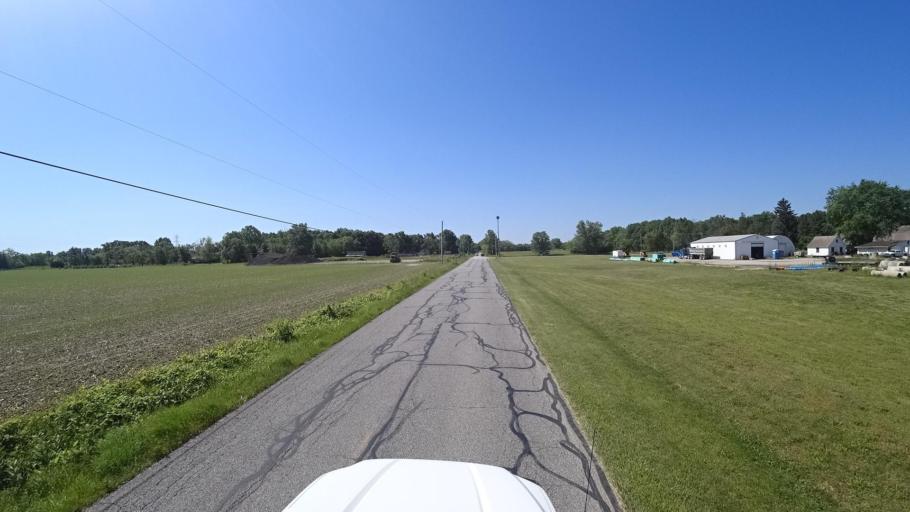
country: US
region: Indiana
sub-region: Porter County
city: Porter
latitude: 41.5882
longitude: -87.1052
